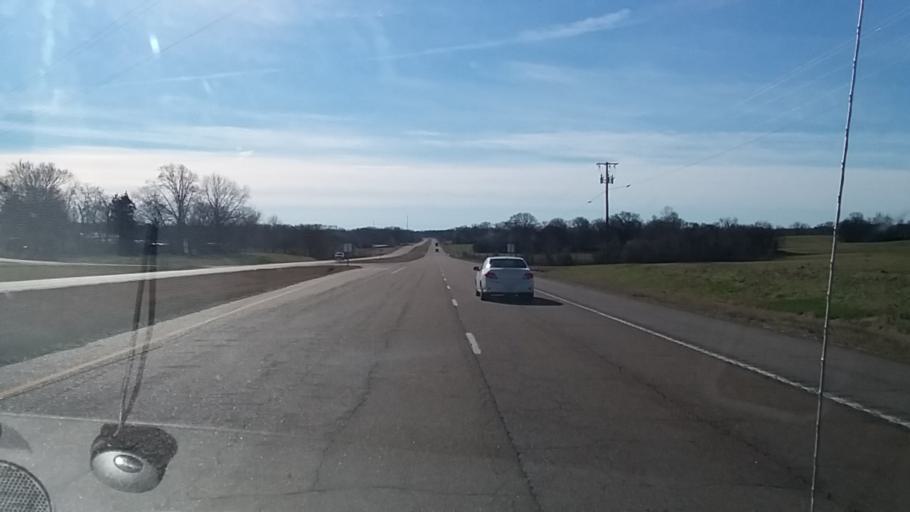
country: US
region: Tennessee
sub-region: Lauderdale County
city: Halls
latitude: 35.9360
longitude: -89.2927
